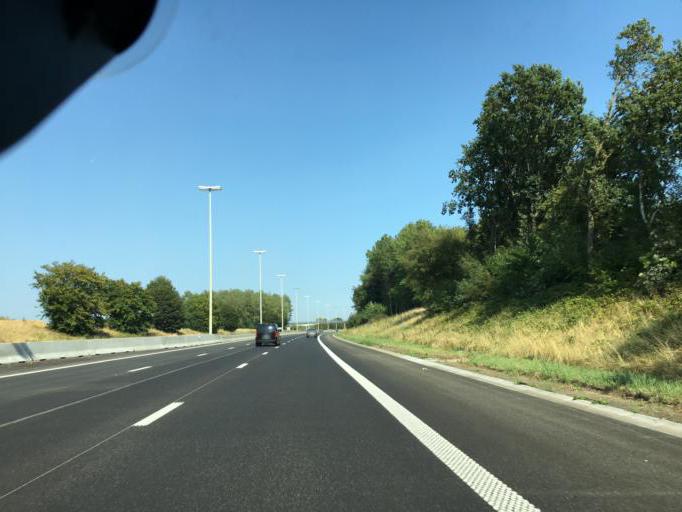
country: BE
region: Wallonia
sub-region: Province de Namur
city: Noville-les-Bois
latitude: 50.5275
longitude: 4.9307
